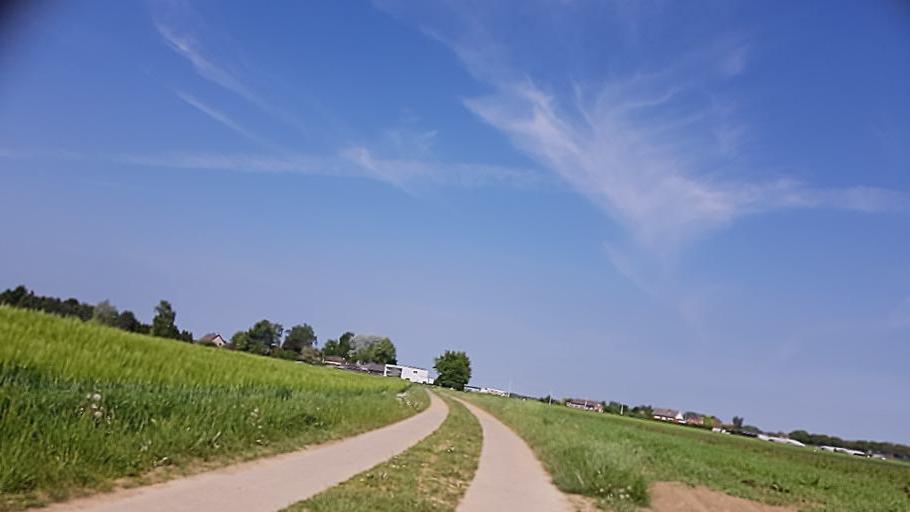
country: BE
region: Flanders
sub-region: Provincie Vlaams-Brabant
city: Huldenberg
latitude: 50.8025
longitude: 4.5687
